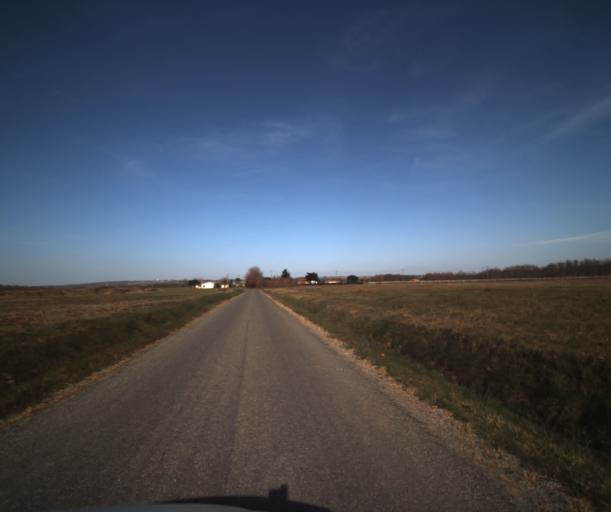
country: FR
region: Midi-Pyrenees
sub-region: Departement du Tarn-et-Garonne
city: Campsas
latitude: 43.9133
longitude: 1.3340
